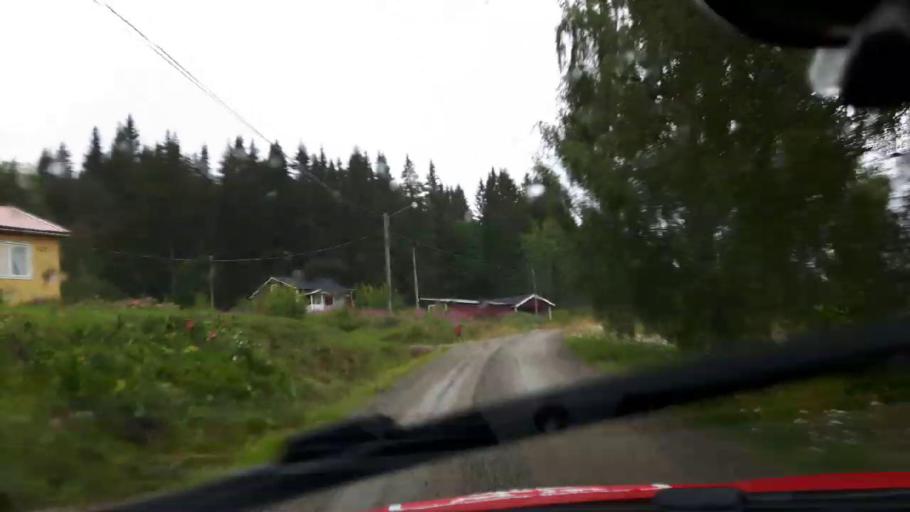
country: SE
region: Jaemtland
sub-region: OEstersunds Kommun
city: Brunflo
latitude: 62.7848
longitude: 14.9676
